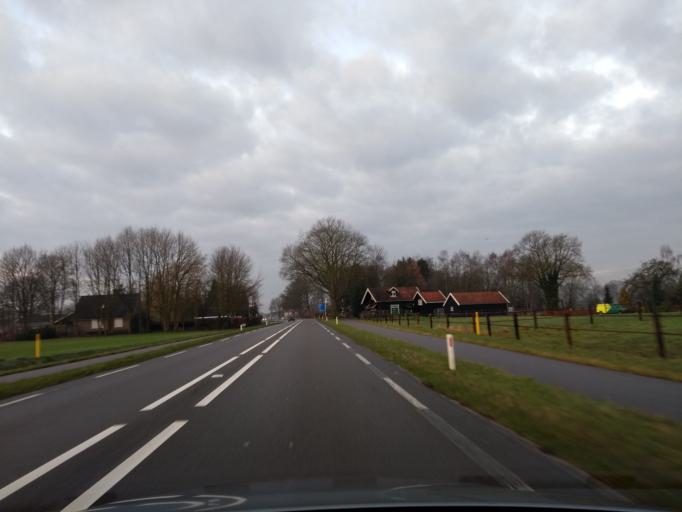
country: NL
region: Gelderland
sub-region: Gemeente Lochem
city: Laren
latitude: 52.2756
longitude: 6.3591
